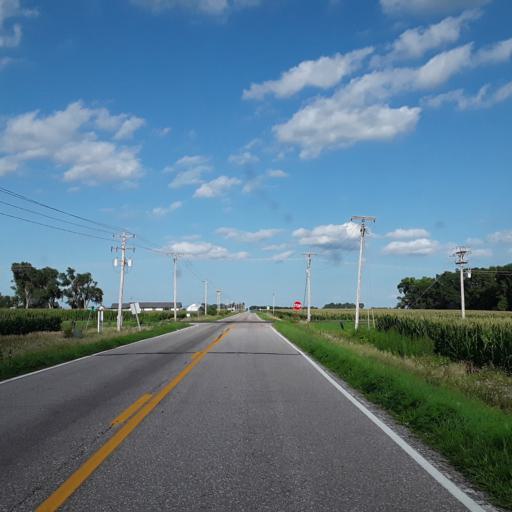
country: US
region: Nebraska
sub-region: Hall County
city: Wood River
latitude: 40.8877
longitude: -98.6091
